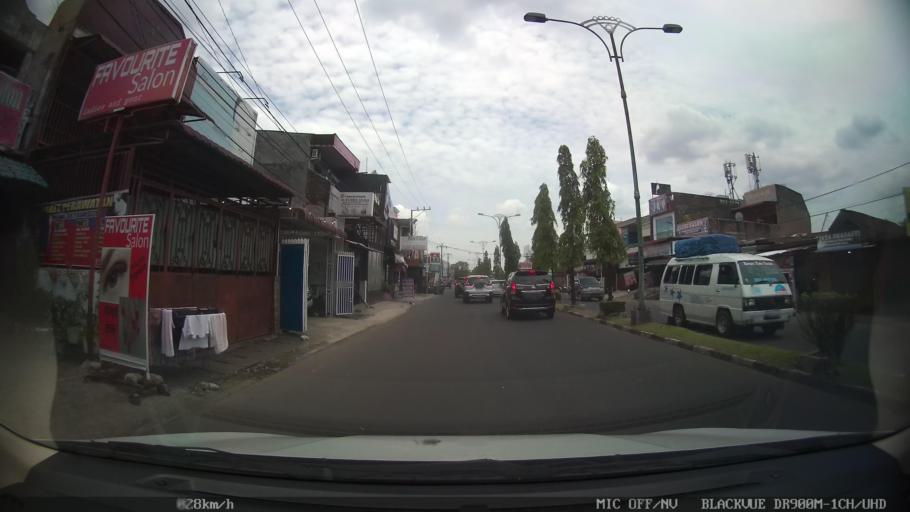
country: ID
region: North Sumatra
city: Medan
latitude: 3.5442
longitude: 98.6572
